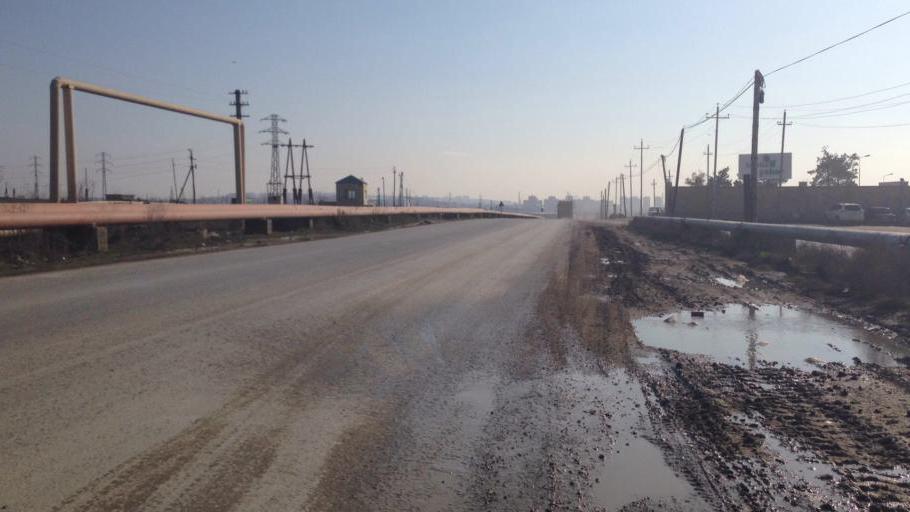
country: AZ
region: Baki
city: Balakhani
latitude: 40.4629
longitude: 49.8890
